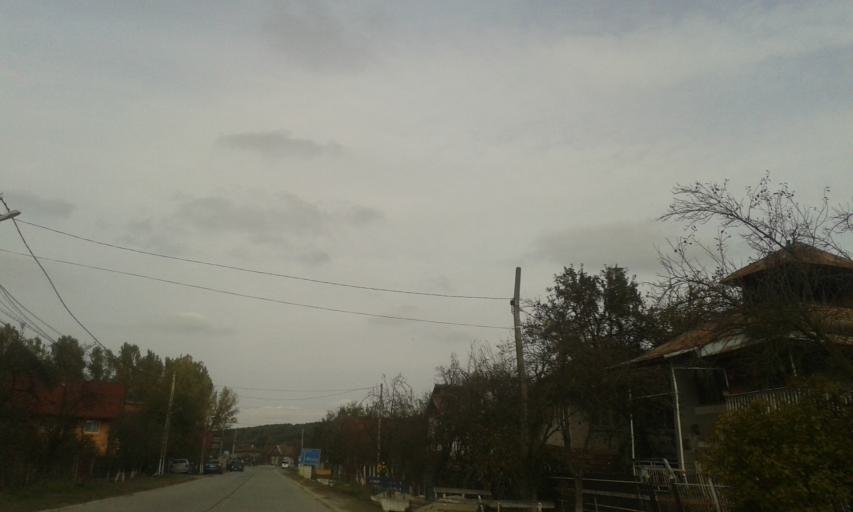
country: RO
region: Gorj
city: Logresti
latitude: 44.8856
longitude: 23.7132
